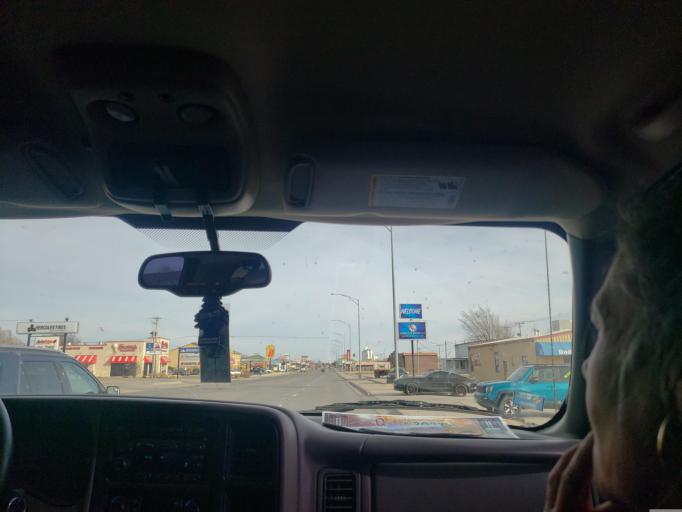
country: US
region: Kansas
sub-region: Ford County
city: Dodge City
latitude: 37.7540
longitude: -100.0398
